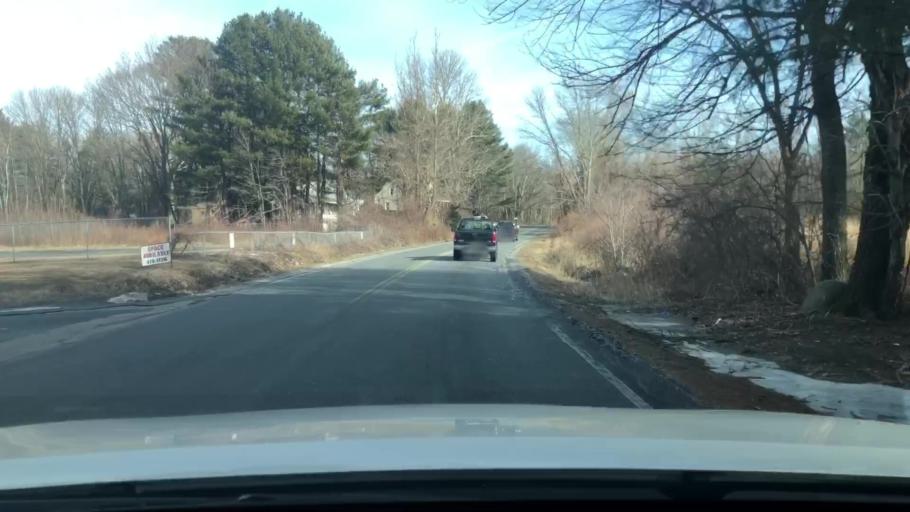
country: US
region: Massachusetts
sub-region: Norfolk County
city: Bellingham
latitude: 42.1020
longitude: -71.5091
